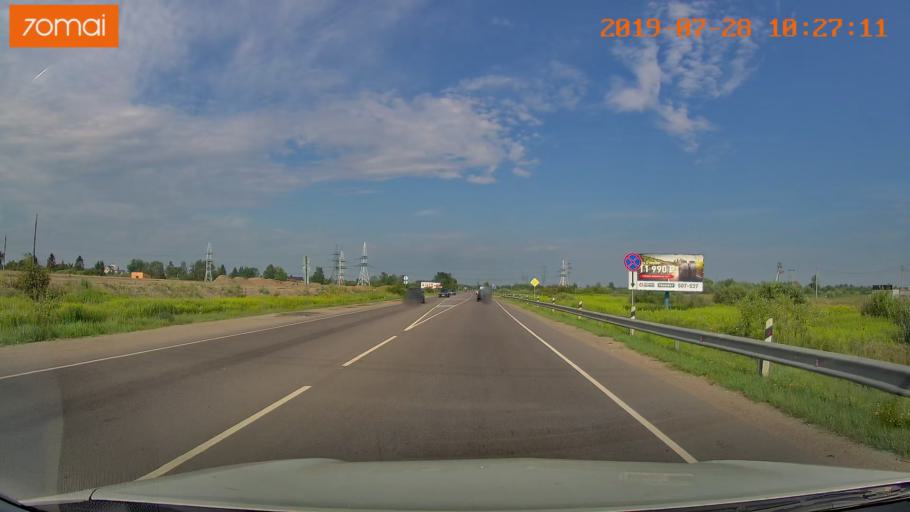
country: RU
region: Kaliningrad
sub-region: Gorod Kaliningrad
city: Kaliningrad
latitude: 54.7699
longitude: 20.5222
